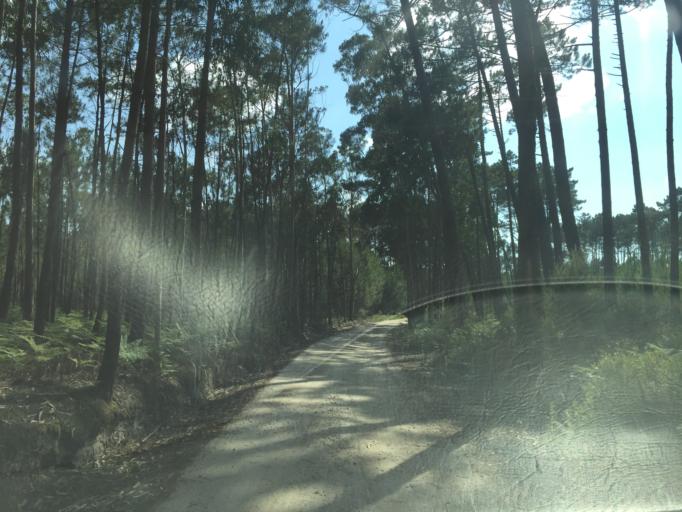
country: PT
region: Leiria
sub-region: Leiria
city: Monte Redondo
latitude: 39.9636
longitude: -8.8054
